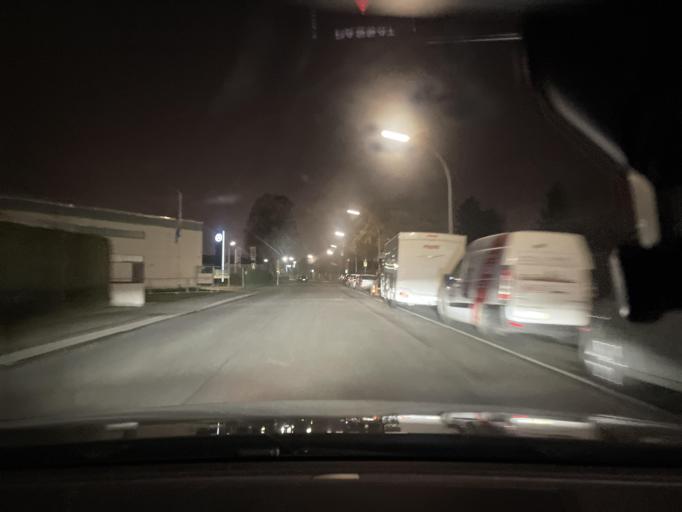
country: DE
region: North Rhine-Westphalia
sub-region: Regierungsbezirk Dusseldorf
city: Korschenbroich
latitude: 51.2309
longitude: 6.4793
